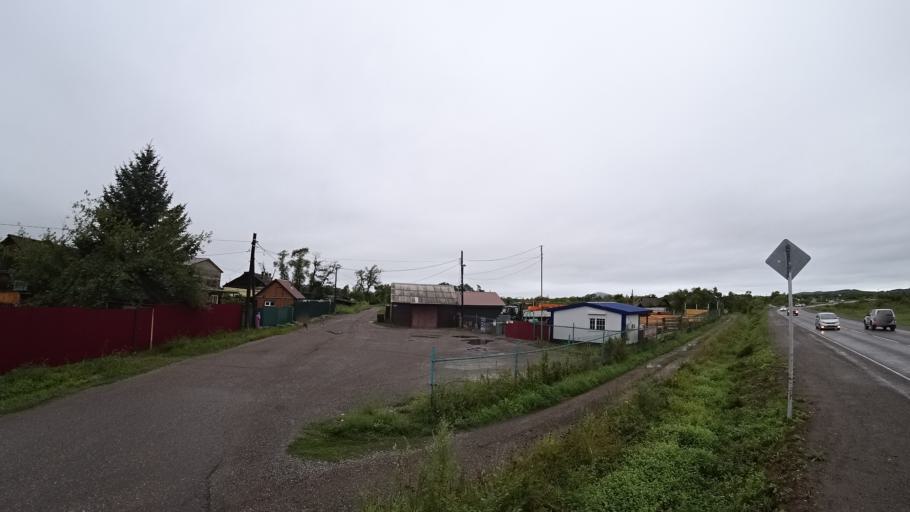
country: RU
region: Primorskiy
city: Monastyrishche
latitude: 44.2111
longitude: 132.4495
